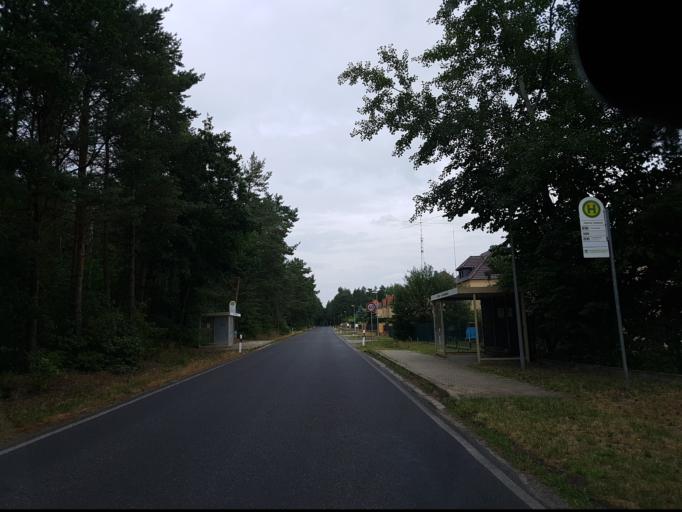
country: DE
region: Brandenburg
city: Schipkau
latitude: 51.5308
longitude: 13.8974
